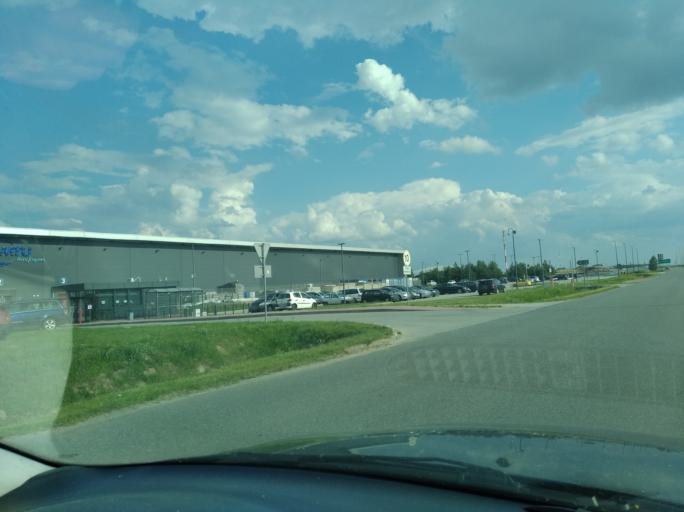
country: PL
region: Subcarpathian Voivodeship
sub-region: Powiat rzeszowski
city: Wysoka Glogowska
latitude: 50.1207
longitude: 22.0231
